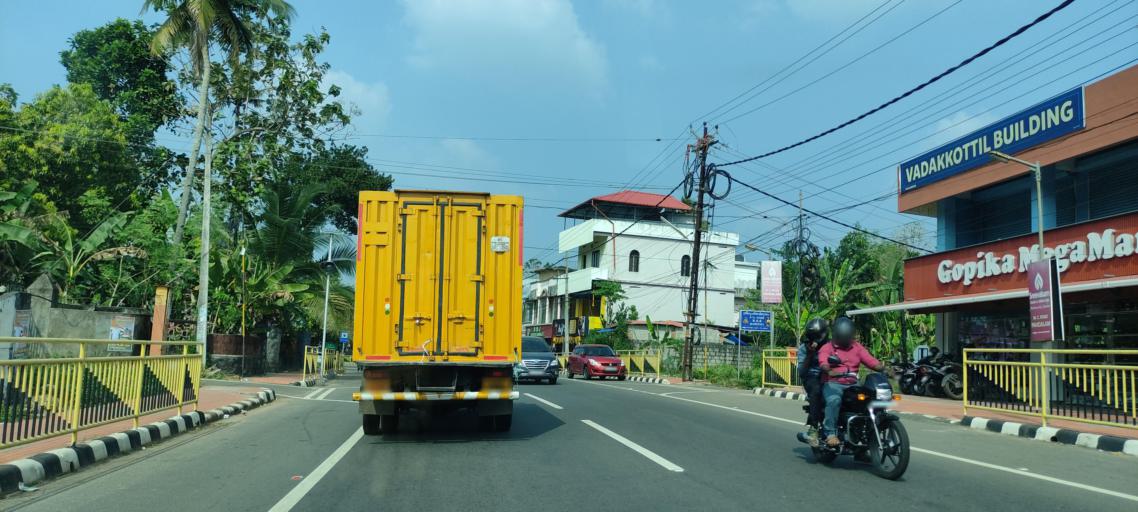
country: IN
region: Kerala
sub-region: Alappuzha
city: Chengannur
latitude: 9.2404
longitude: 76.6727
